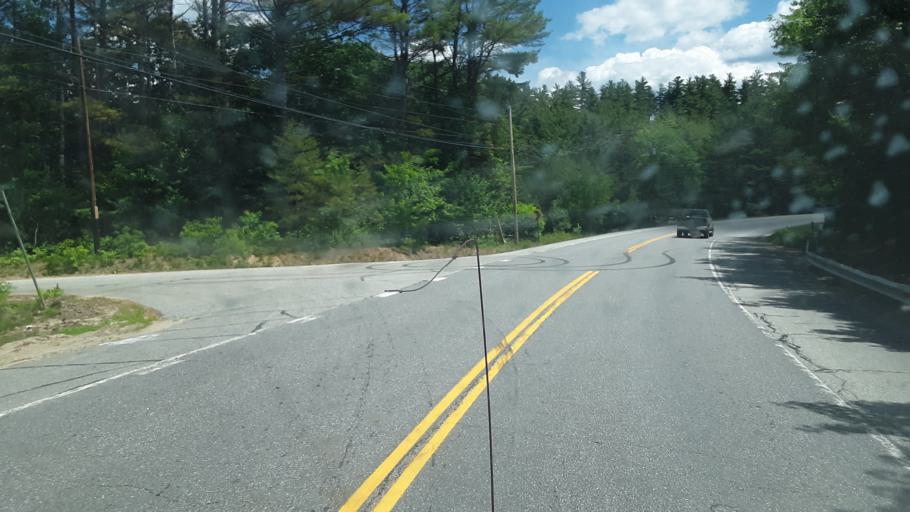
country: US
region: Maine
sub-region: Oxford County
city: Rumford
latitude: 44.5067
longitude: -70.6750
